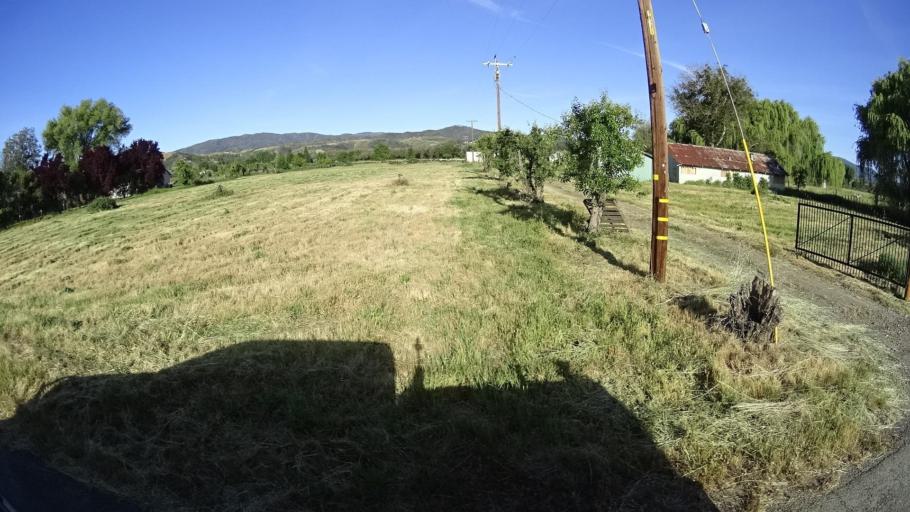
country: US
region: California
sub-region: Lake County
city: Lakeport
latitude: 39.0728
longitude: -122.9495
